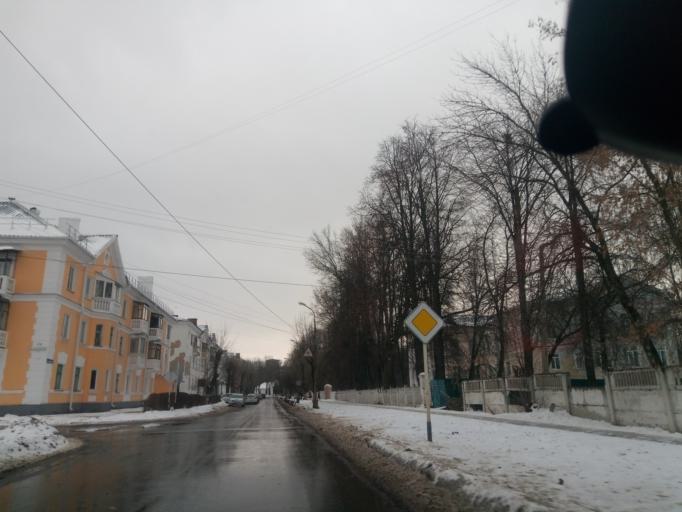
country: RU
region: Tula
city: Novomoskovsk
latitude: 54.0135
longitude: 38.2834
